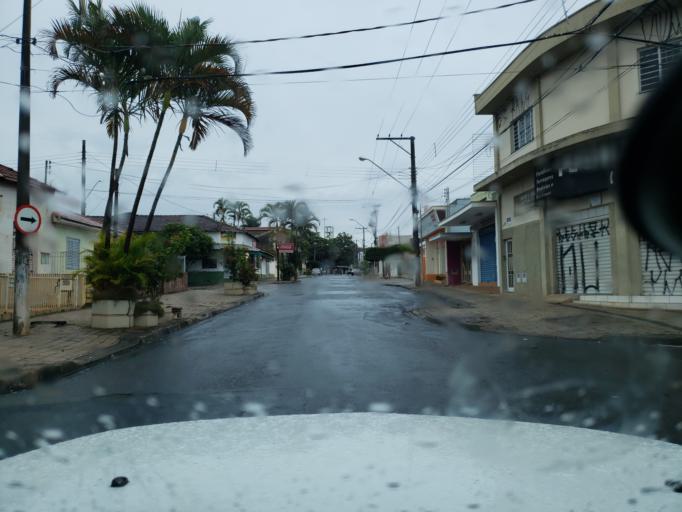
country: BR
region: Sao Paulo
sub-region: Moji-Guacu
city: Mogi-Gaucu
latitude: -22.3617
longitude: -46.9444
